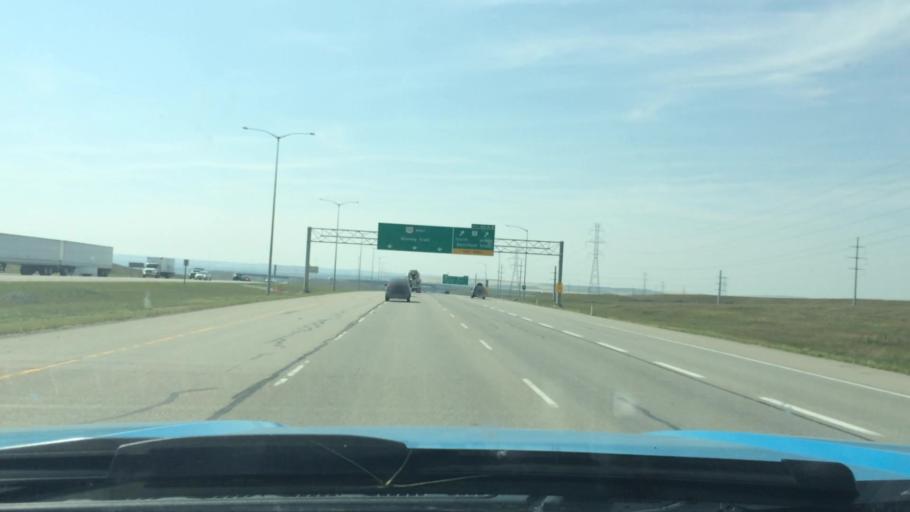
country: CA
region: Alberta
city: Airdrie
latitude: 51.1758
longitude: -113.9809
